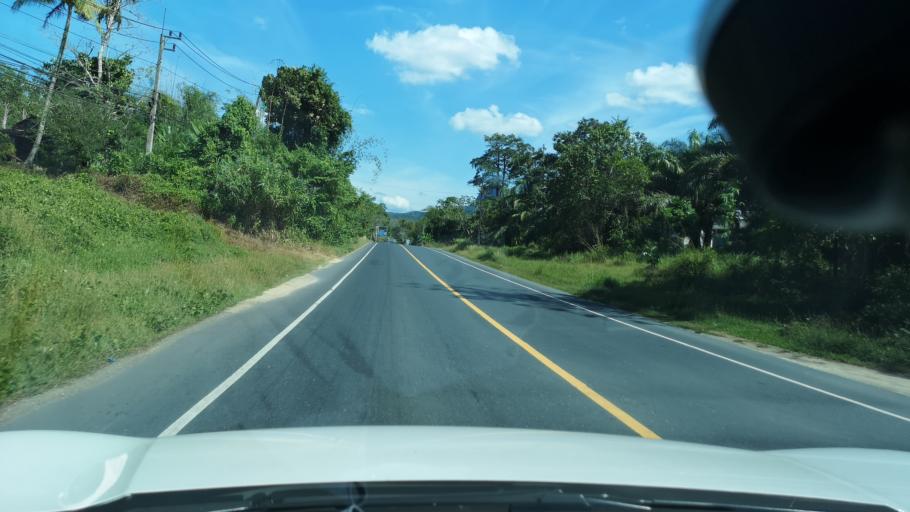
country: TH
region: Phangnga
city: Phang Nga
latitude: 8.5331
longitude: 98.5084
